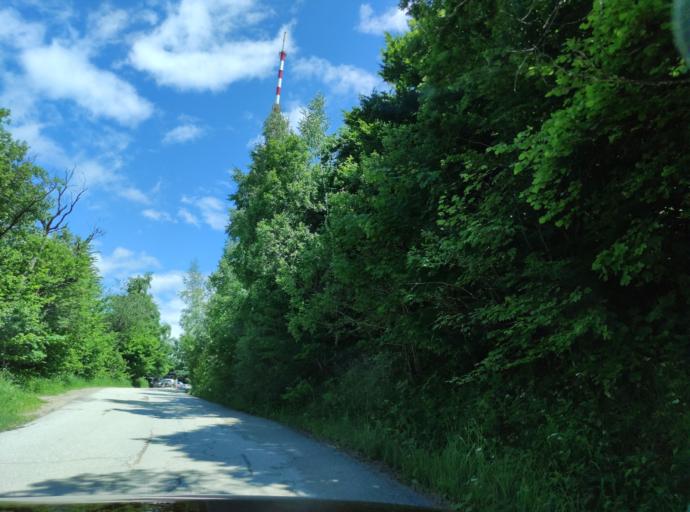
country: BG
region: Sofia-Capital
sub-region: Stolichna Obshtina
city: Sofia
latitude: 42.6353
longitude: 23.2431
